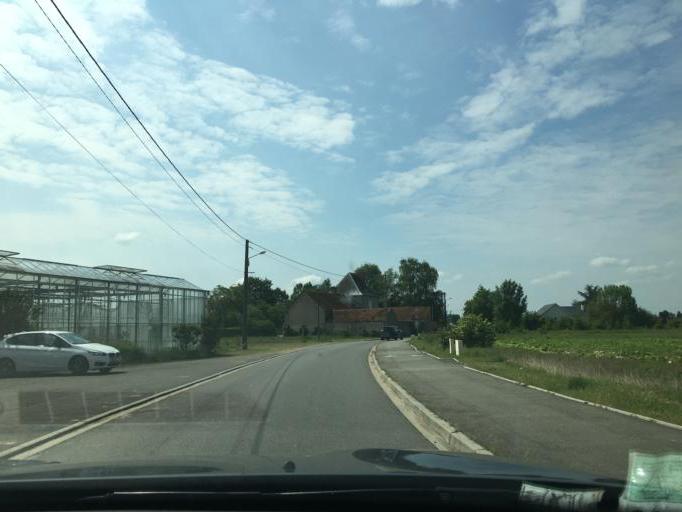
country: FR
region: Centre
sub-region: Departement du Loiret
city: Saint-Denis-en-Val
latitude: 47.8886
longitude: 1.9601
